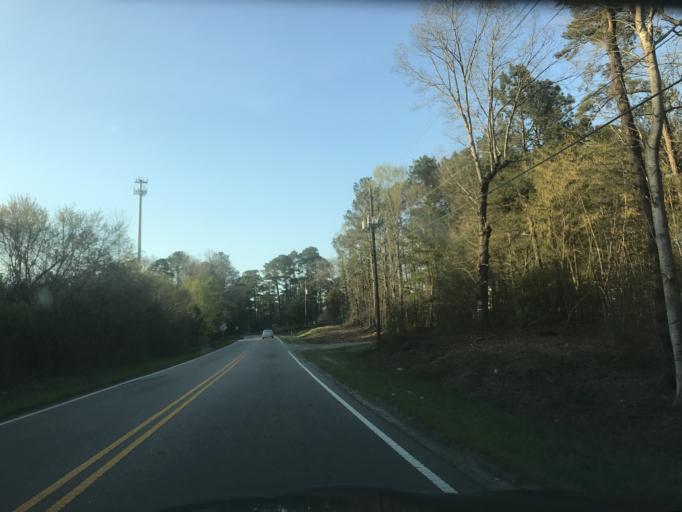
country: US
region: North Carolina
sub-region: Wake County
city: Knightdale
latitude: 35.7506
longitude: -78.5348
